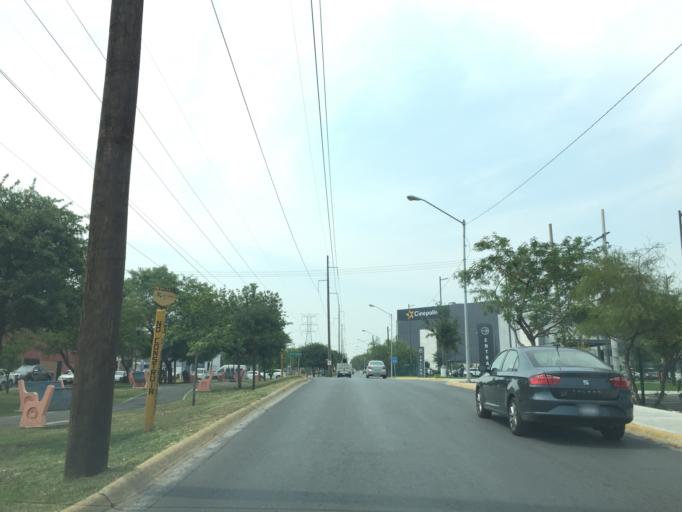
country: MX
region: Nuevo Leon
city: Guadalupe
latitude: 25.7179
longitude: -100.2204
